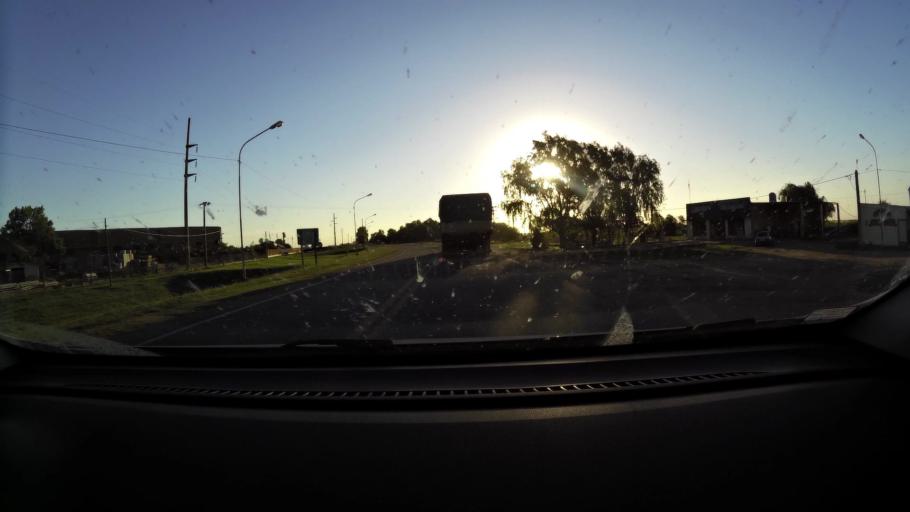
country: AR
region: Cordoba
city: Pozo del Molle
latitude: -32.0237
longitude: -62.9262
